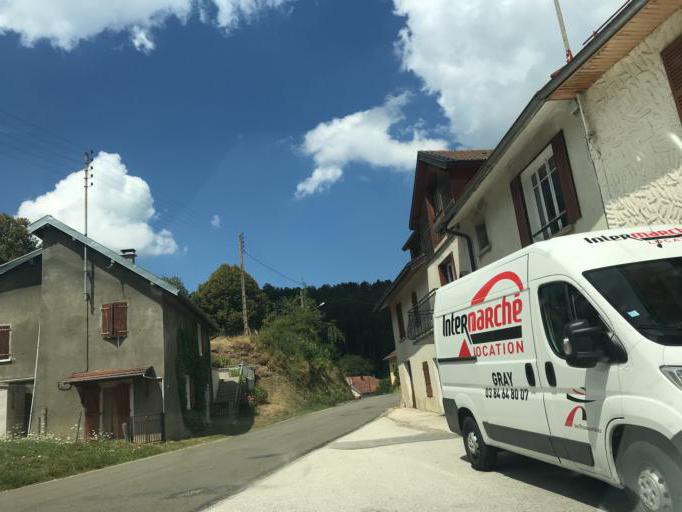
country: FR
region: Franche-Comte
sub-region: Departement du Jura
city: Clairvaux-les-Lacs
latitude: 46.5268
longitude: 5.7933
